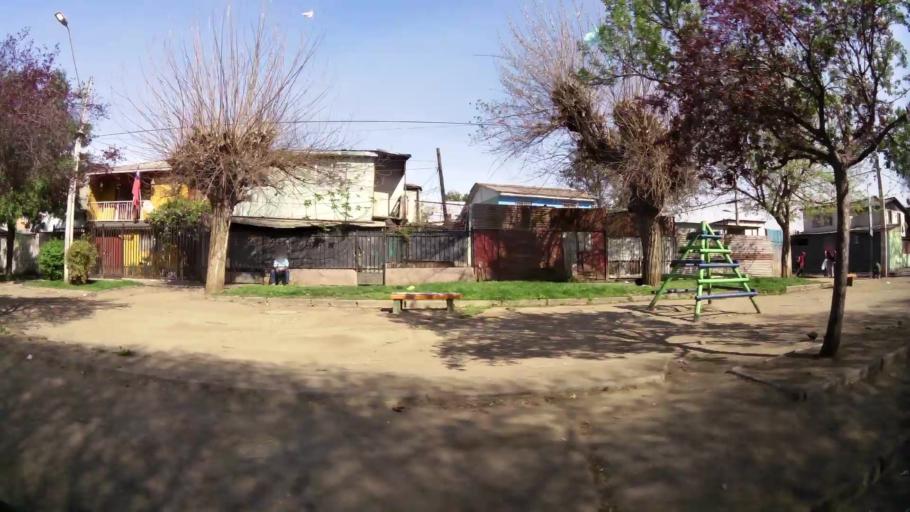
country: CL
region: Santiago Metropolitan
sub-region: Provincia de Santiago
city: Lo Prado
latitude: -33.4173
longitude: -70.7330
